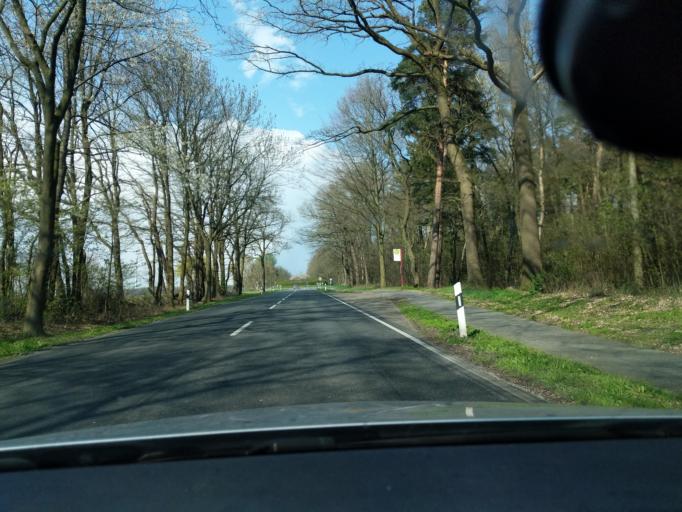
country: DE
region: Lower Saxony
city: Harsefeld
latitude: 53.4732
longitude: 9.4935
